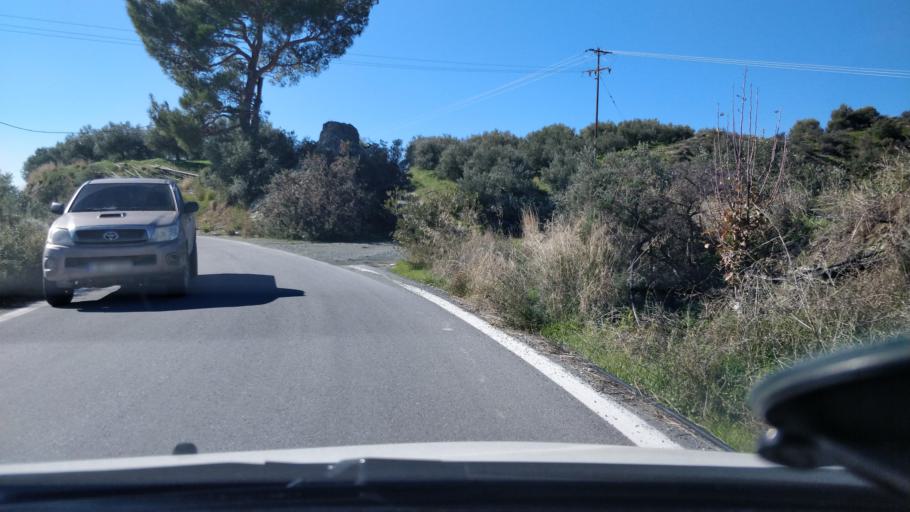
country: GR
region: Crete
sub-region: Nomos Irakleiou
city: Kastelli
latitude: 35.0126
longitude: 25.4459
